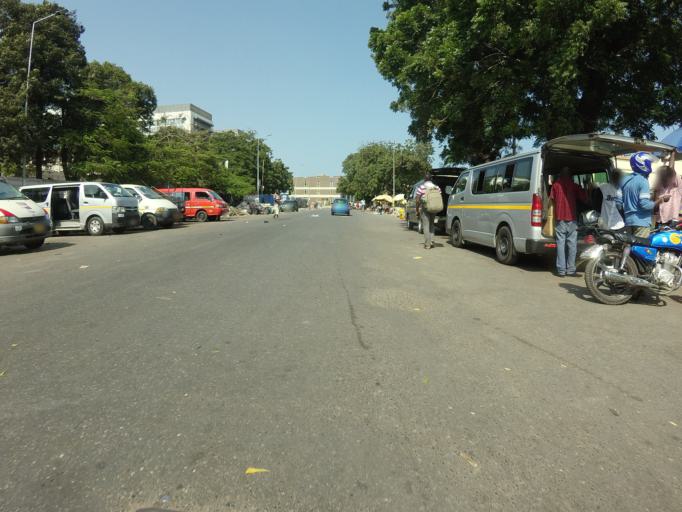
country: GH
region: Greater Accra
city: Accra
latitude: 5.5506
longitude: -0.2054
